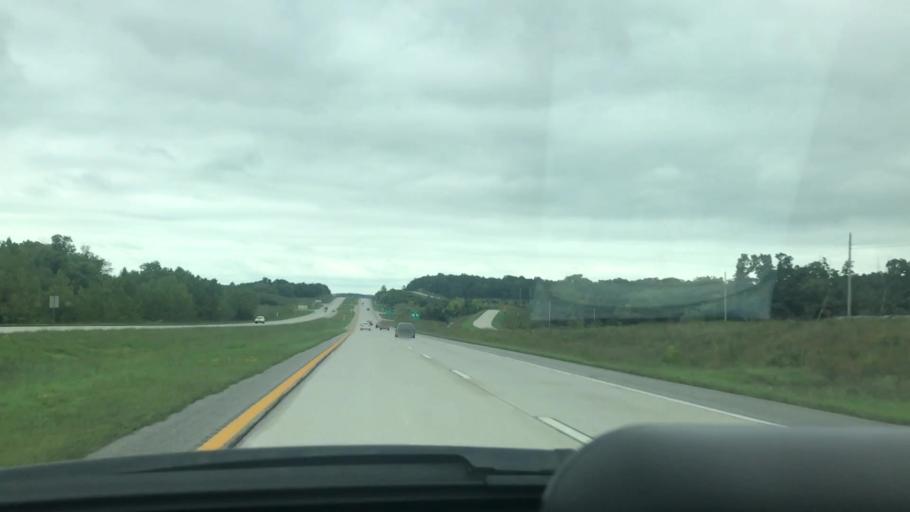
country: US
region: Missouri
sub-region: Greene County
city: Fair Grove
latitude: 37.5120
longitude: -93.1387
